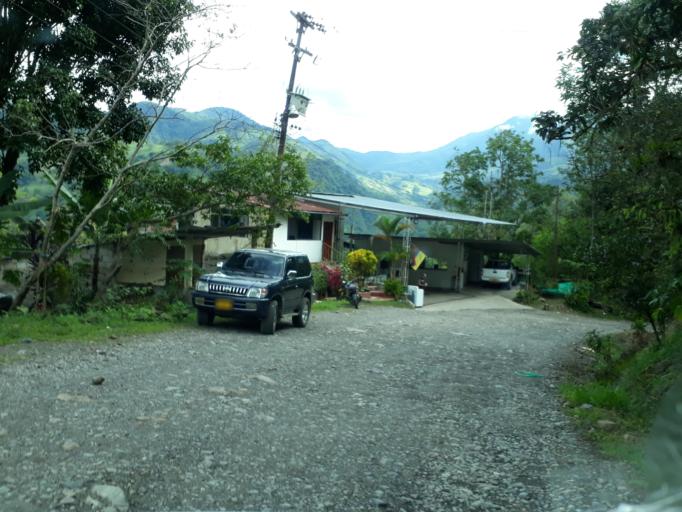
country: CO
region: Boyaca
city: Santa Maria
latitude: 4.7613
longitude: -73.3228
